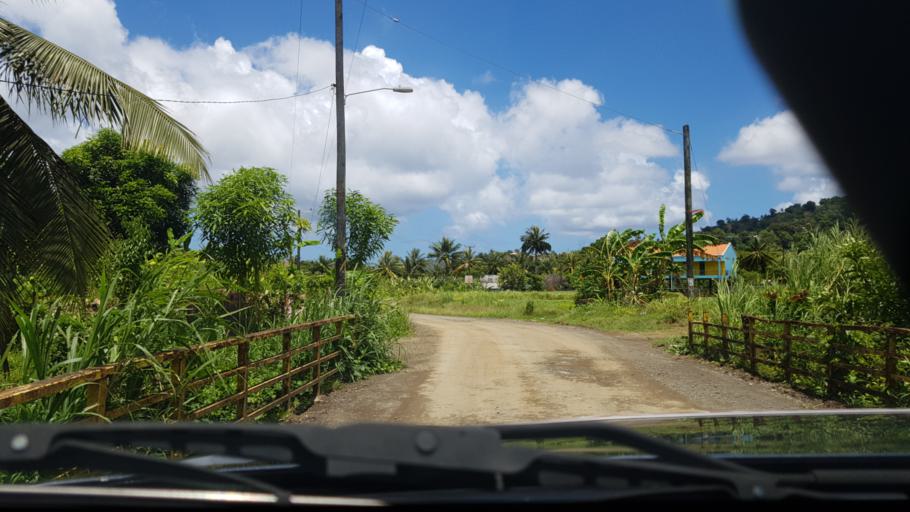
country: LC
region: Anse-la-Raye
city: Anse La Raye
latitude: 13.9490
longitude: -60.9937
